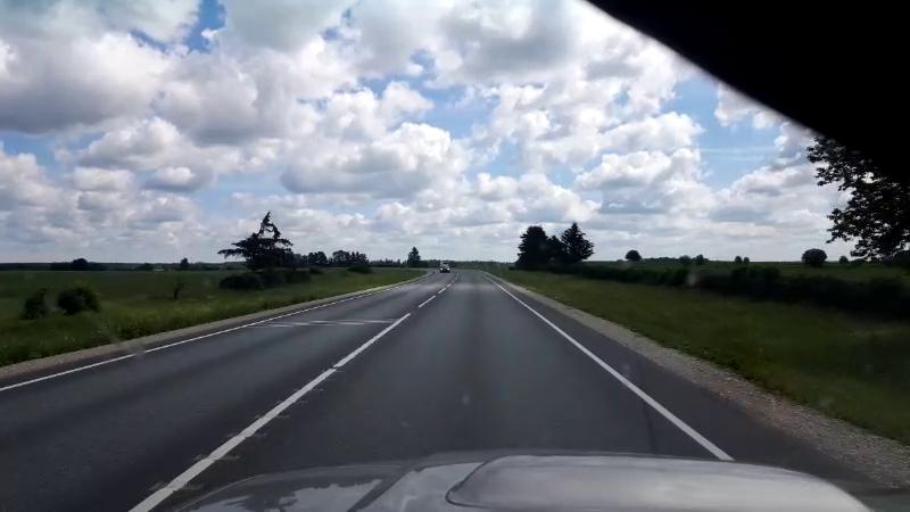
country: EE
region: Laeaene-Virumaa
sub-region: Tapa vald
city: Tapa
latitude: 59.2542
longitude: 25.9883
